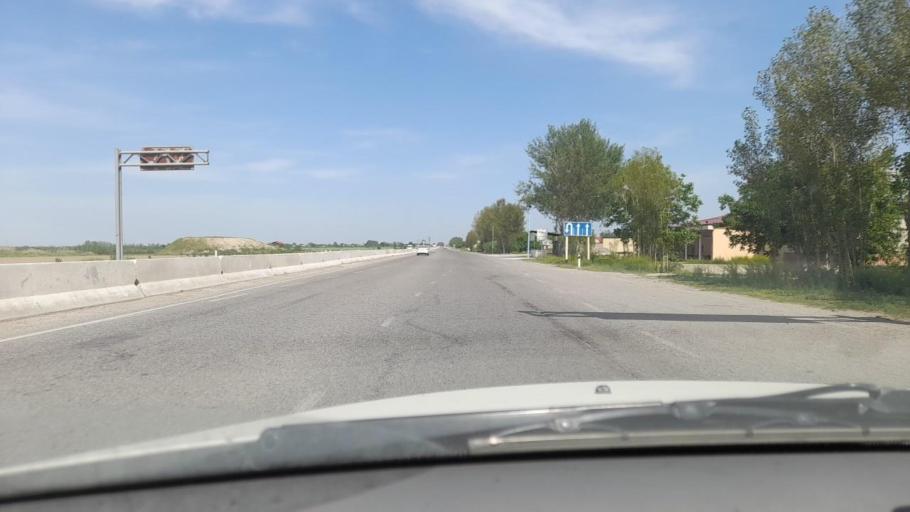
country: UZ
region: Samarqand
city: Kattaqo'rg'on
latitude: 39.9181
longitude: 66.3323
